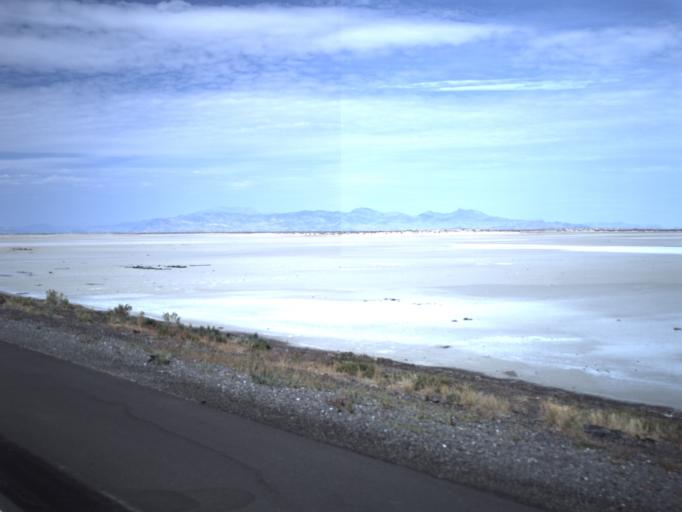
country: US
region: Utah
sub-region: Tooele County
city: Wendover
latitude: 40.7305
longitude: -113.4449
